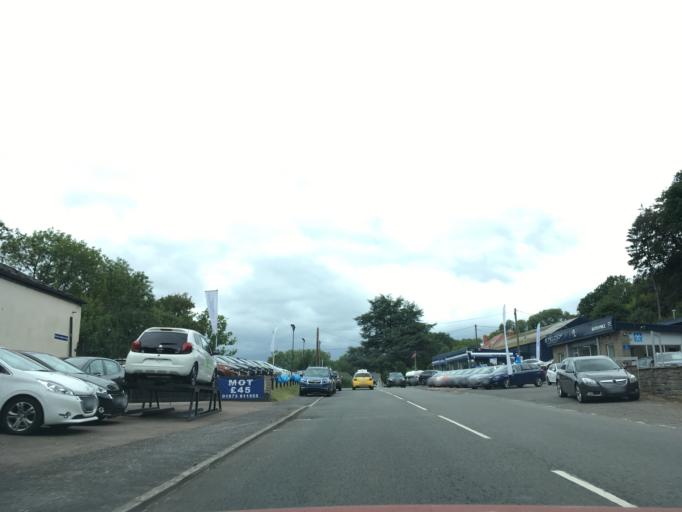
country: GB
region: Wales
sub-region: Monmouthshire
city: Gilwern
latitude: 51.8377
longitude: -3.0822
